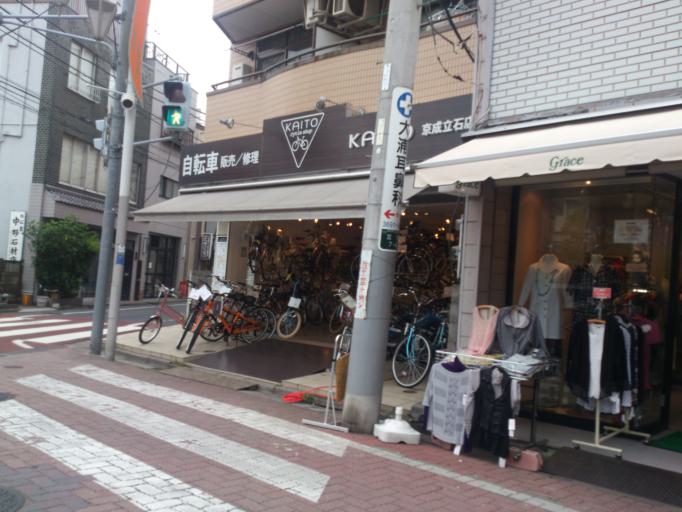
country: JP
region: Chiba
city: Matsudo
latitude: 35.7398
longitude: 139.8489
